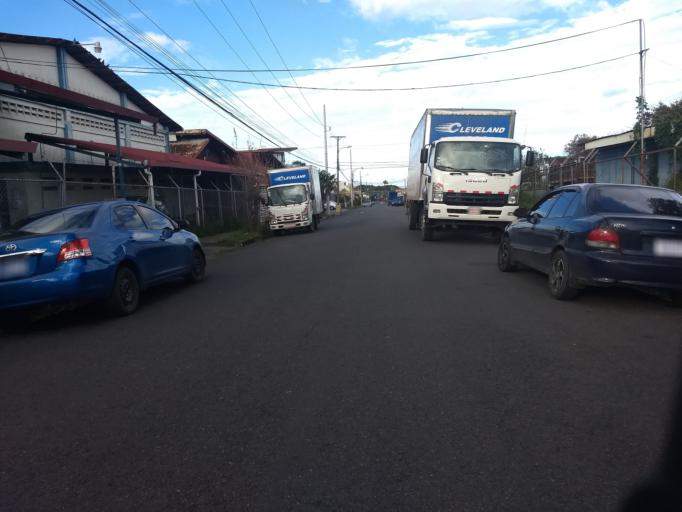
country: CR
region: San Jose
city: San Juan
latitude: 9.9572
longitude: -84.0814
